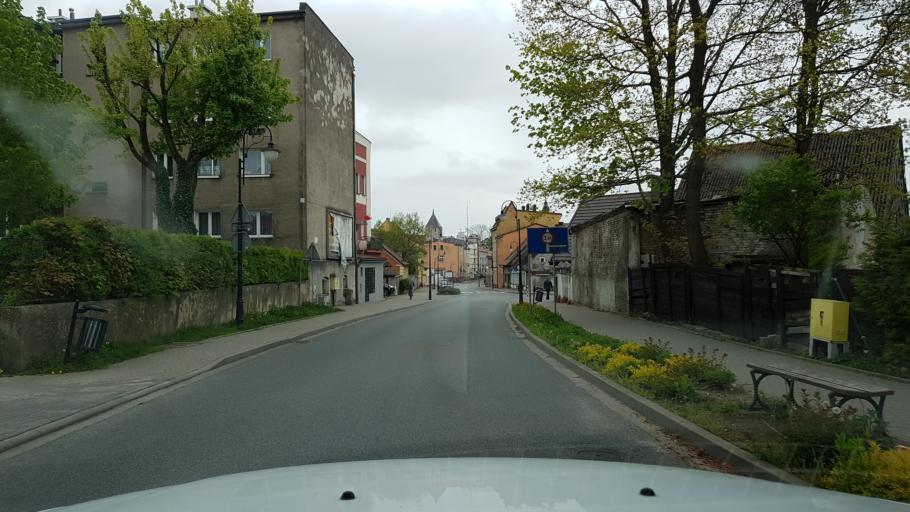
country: PL
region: West Pomeranian Voivodeship
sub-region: Powiat slawienski
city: Slawno
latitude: 54.3682
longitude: 16.6795
